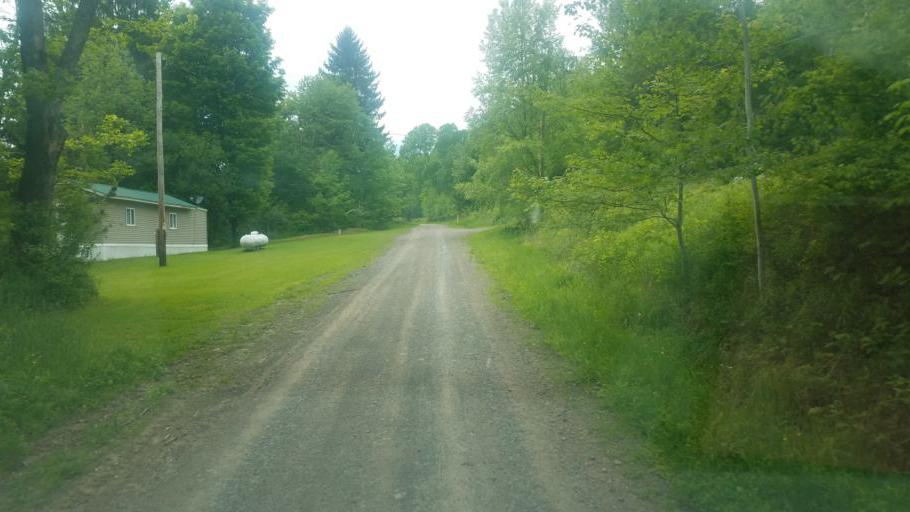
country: US
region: Pennsylvania
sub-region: Tioga County
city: Westfield
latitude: 41.9284
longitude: -77.6925
